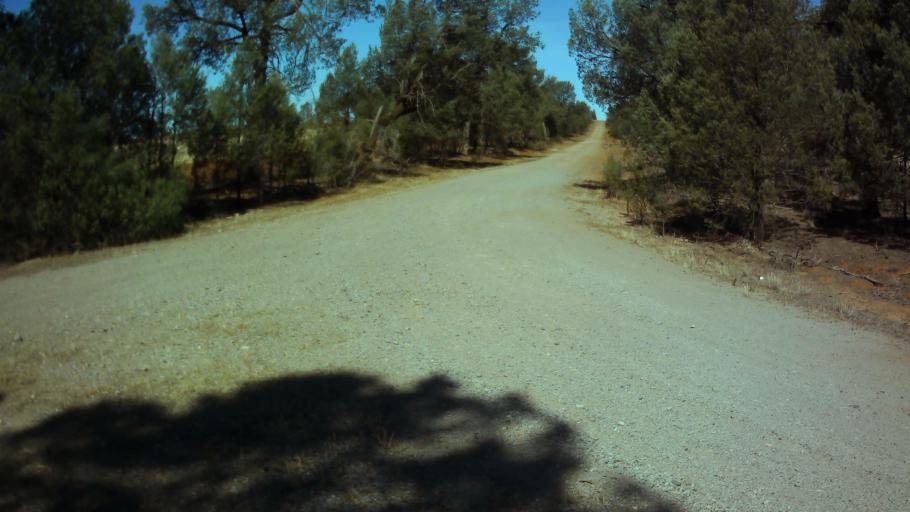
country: AU
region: New South Wales
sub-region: Weddin
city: Grenfell
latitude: -33.7813
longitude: 147.7531
